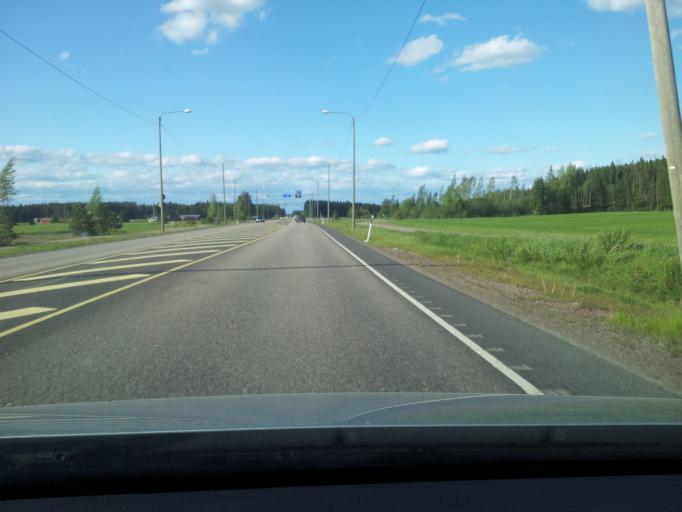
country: FI
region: Kymenlaakso
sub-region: Kouvola
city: Elimaeki
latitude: 60.7698
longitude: 26.4771
